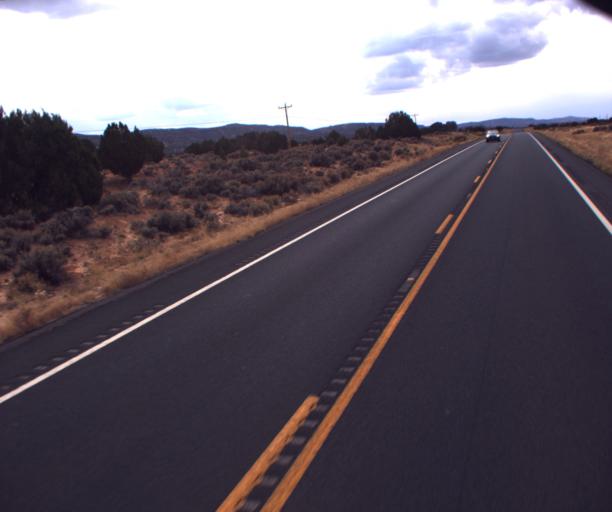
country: US
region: Arizona
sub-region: Navajo County
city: Kayenta
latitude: 36.5024
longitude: -110.6150
